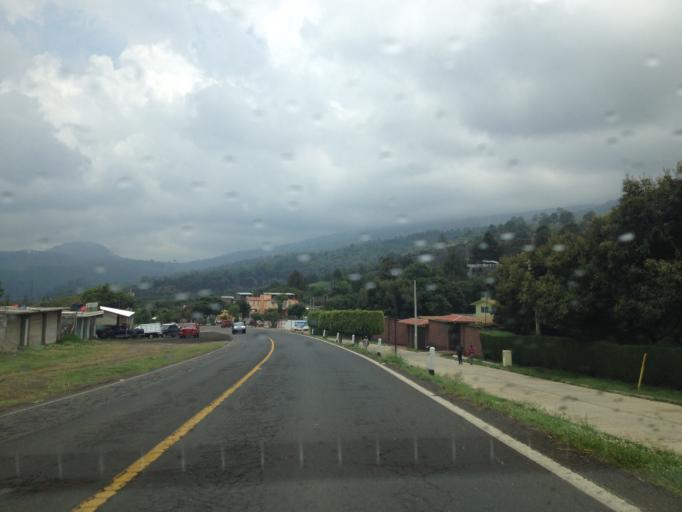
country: MX
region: Michoacan
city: Tingambato
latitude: 19.5072
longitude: -101.8554
